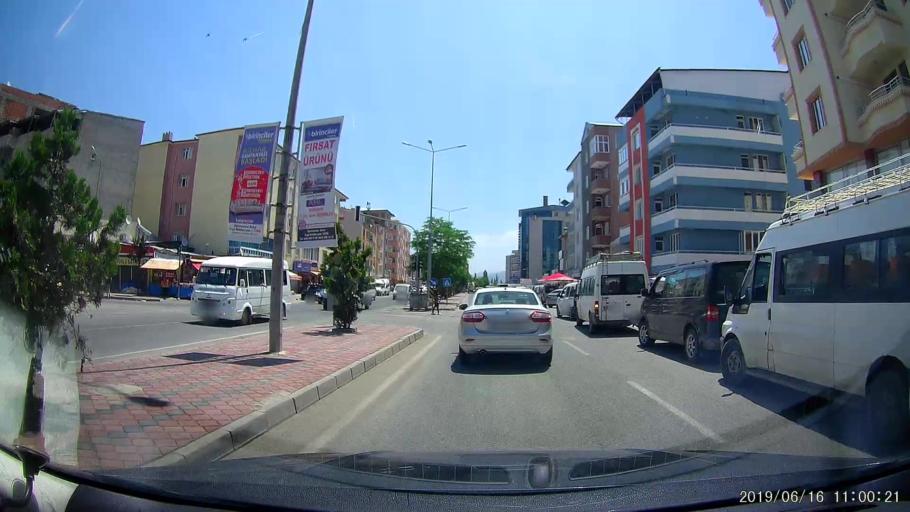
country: TR
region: Igdir
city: Igdir
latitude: 39.9186
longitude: 44.0433
